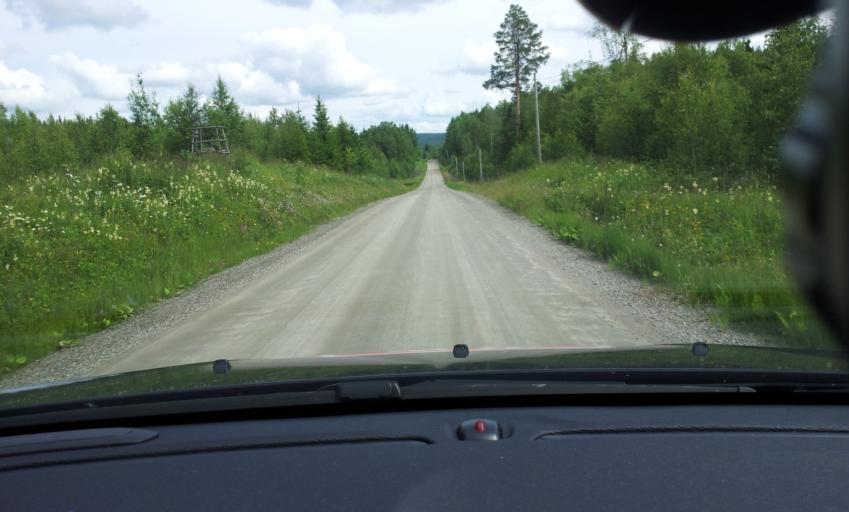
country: SE
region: Jaemtland
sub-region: OEstersunds Kommun
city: Brunflo
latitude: 62.9412
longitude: 14.9739
